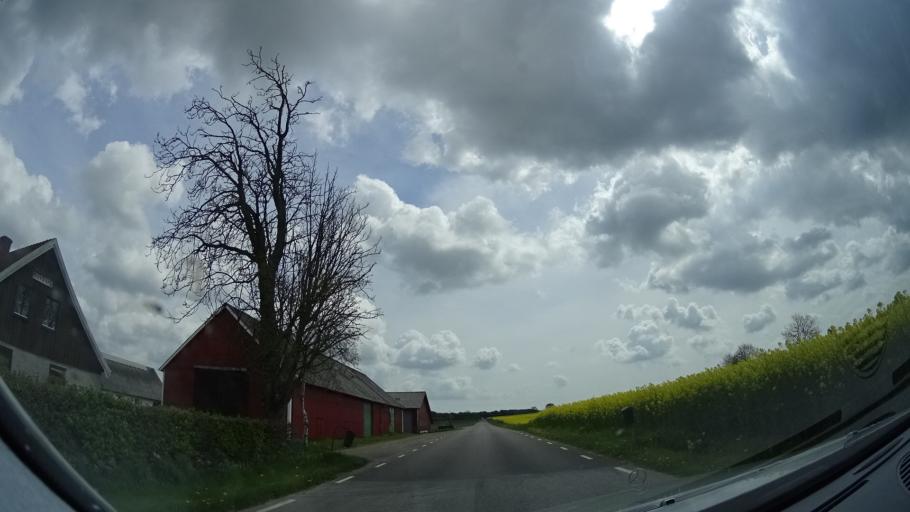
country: SE
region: Skane
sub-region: Hoors Kommun
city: Loberod
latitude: 55.7980
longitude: 13.4818
